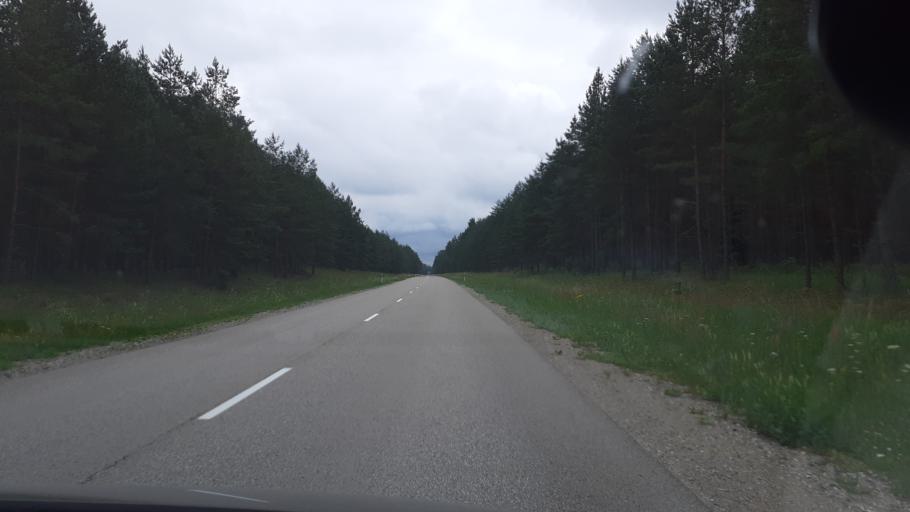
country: LV
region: Ventspils Rajons
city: Piltene
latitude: 57.1170
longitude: 21.7507
